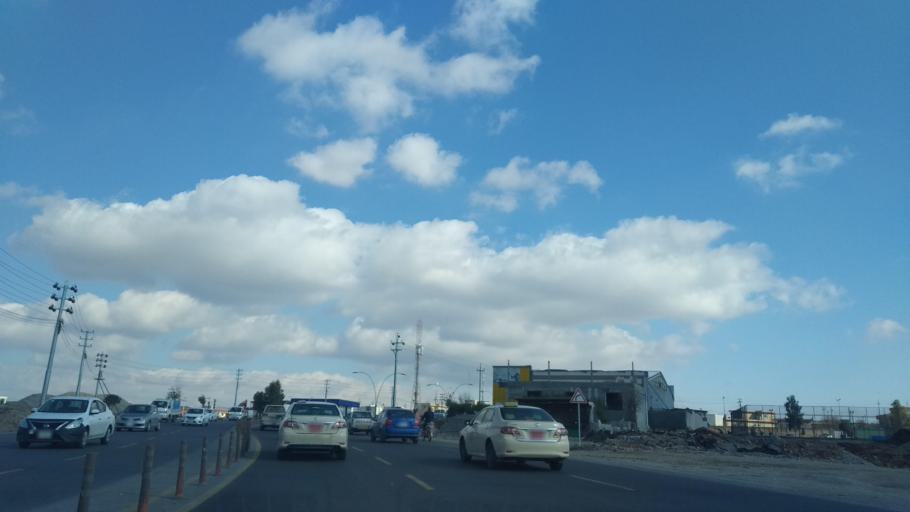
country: IQ
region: Arbil
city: Erbil
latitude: 36.2062
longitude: 44.1298
